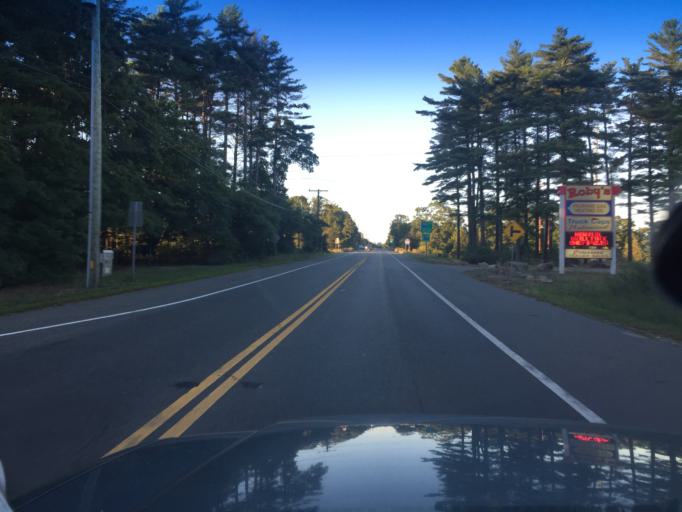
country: US
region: Massachusetts
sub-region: Plymouth County
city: West Wareham
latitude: 41.8027
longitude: -70.7724
